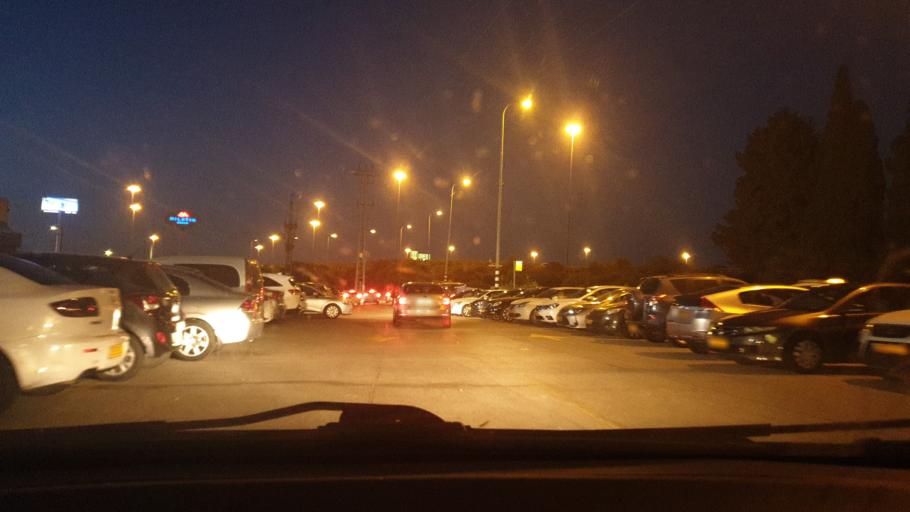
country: IL
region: Central District
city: Bene 'Ayish
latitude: 31.7999
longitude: 34.7620
